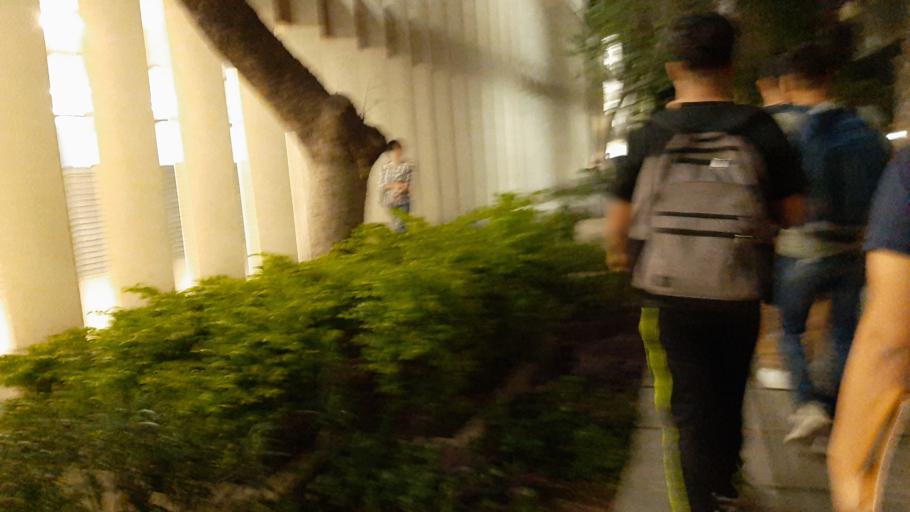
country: MX
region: Nuevo Leon
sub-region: San Nicolas de los Garza
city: San Nicolas de los Garza
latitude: 25.7255
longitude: -100.3118
